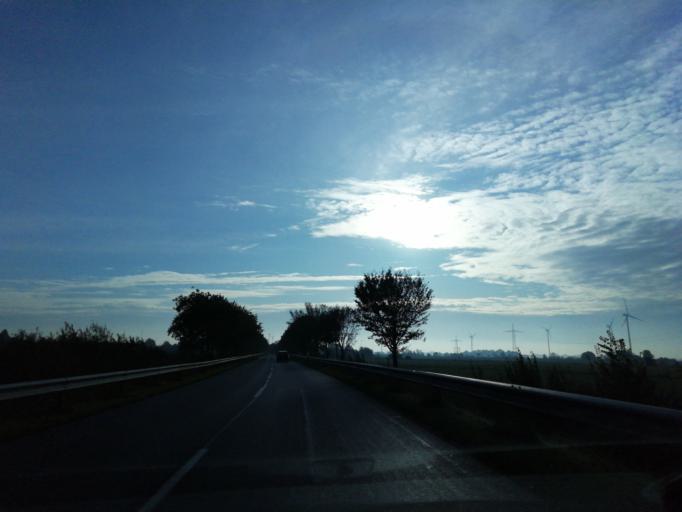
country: DE
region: Lower Saxony
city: Sillenstede
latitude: 53.6237
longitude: 8.0171
